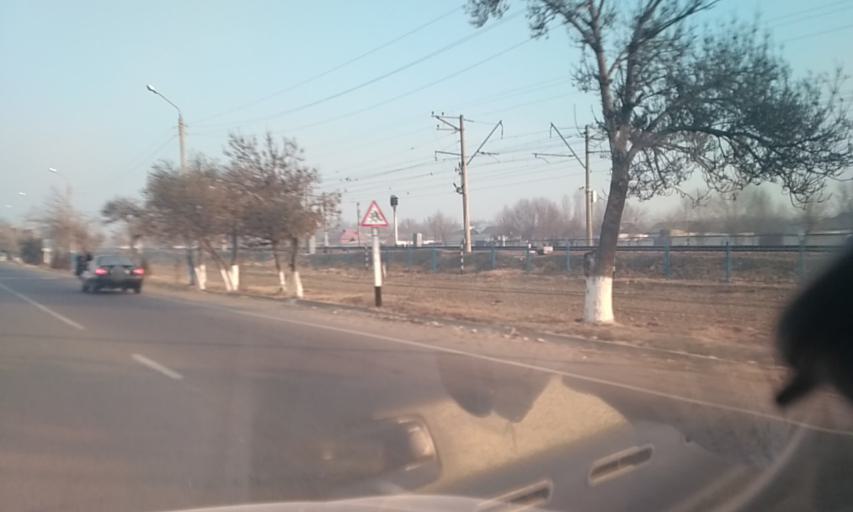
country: UZ
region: Sirdaryo
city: Guliston
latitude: 40.5152
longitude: 68.7582
